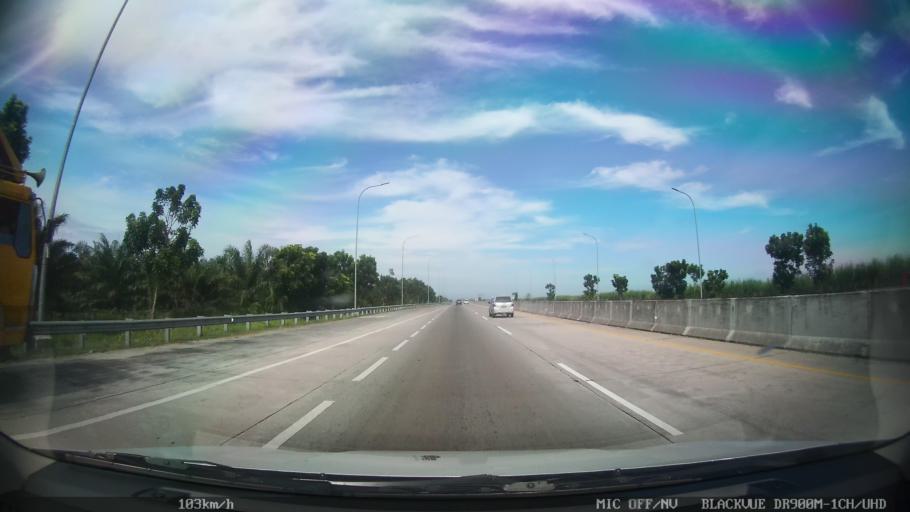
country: ID
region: North Sumatra
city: Medan
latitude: 3.6379
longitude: 98.6337
